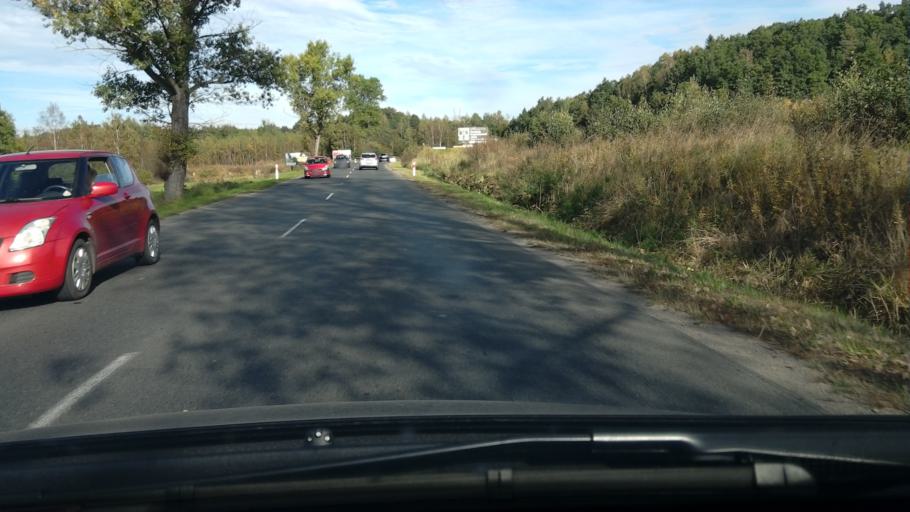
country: PL
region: Lower Silesian Voivodeship
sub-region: Powiat jeleniogorski
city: Myslakowice
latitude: 50.8633
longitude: 15.7739
